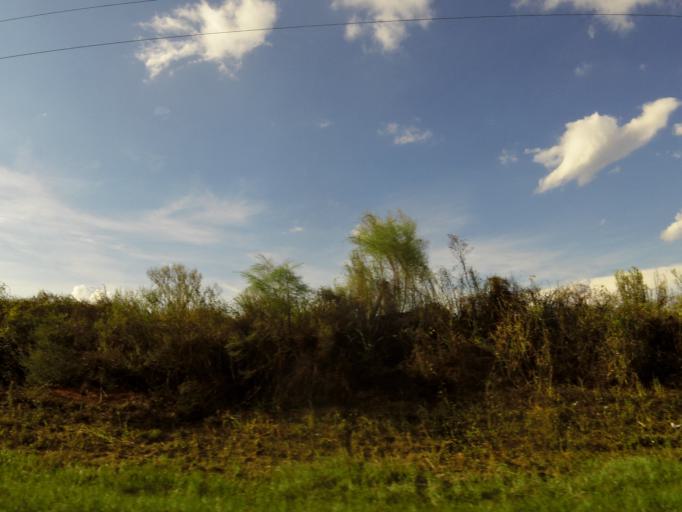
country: US
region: Georgia
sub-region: Brooks County
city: Quitman
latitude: 30.7773
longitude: -83.5988
